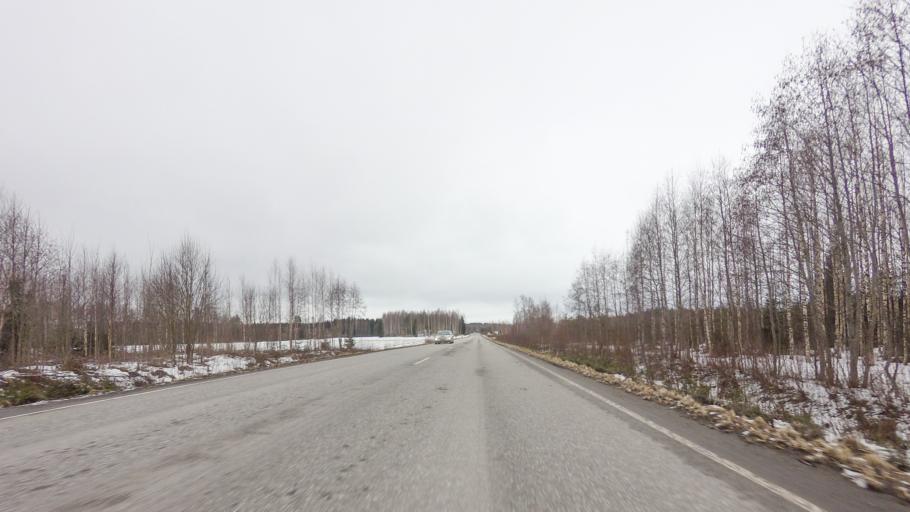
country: FI
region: Southern Savonia
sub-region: Savonlinna
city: Savonlinna
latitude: 61.9020
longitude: 28.9258
